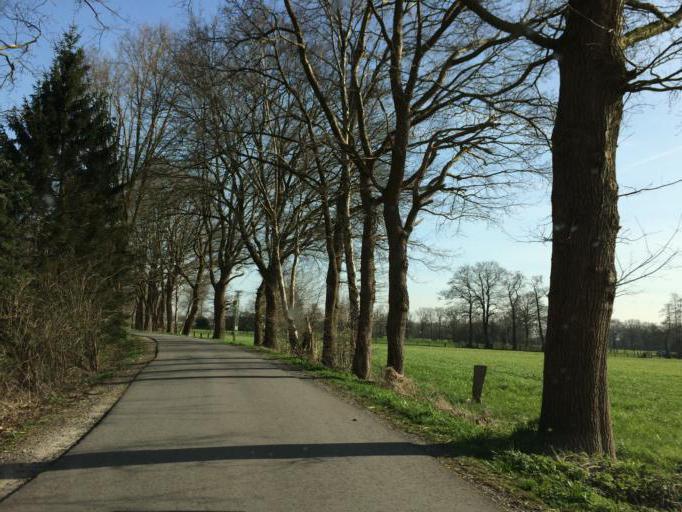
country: DE
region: North Rhine-Westphalia
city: Marl
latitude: 51.6954
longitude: 7.0353
